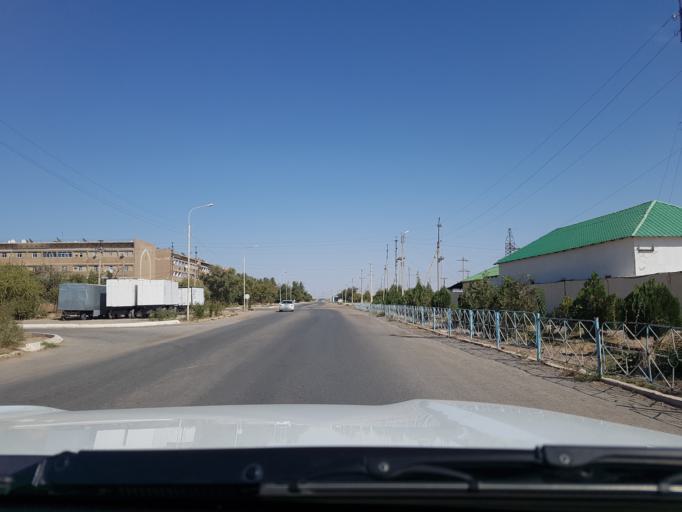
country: IR
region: Razavi Khorasan
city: Sarakhs
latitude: 36.5238
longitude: 61.2229
